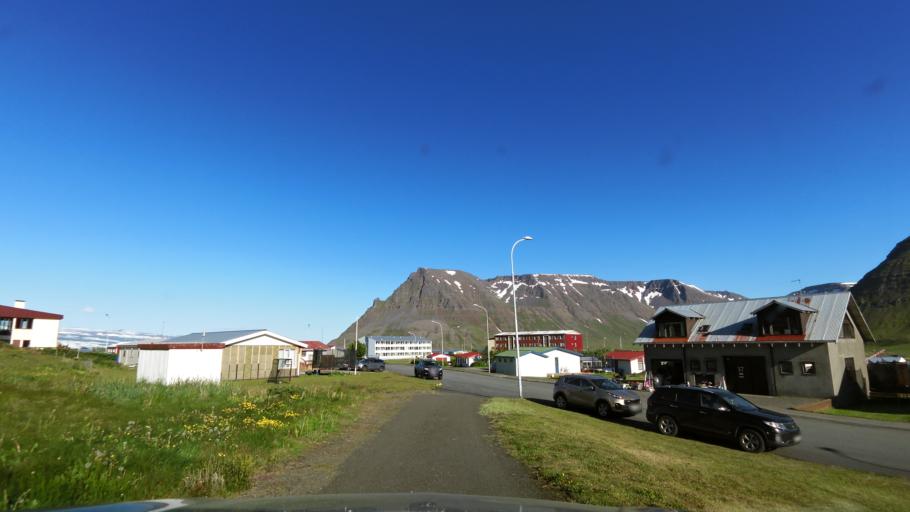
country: IS
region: Westfjords
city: Isafjoerdur
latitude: 66.1604
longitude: -23.2650
